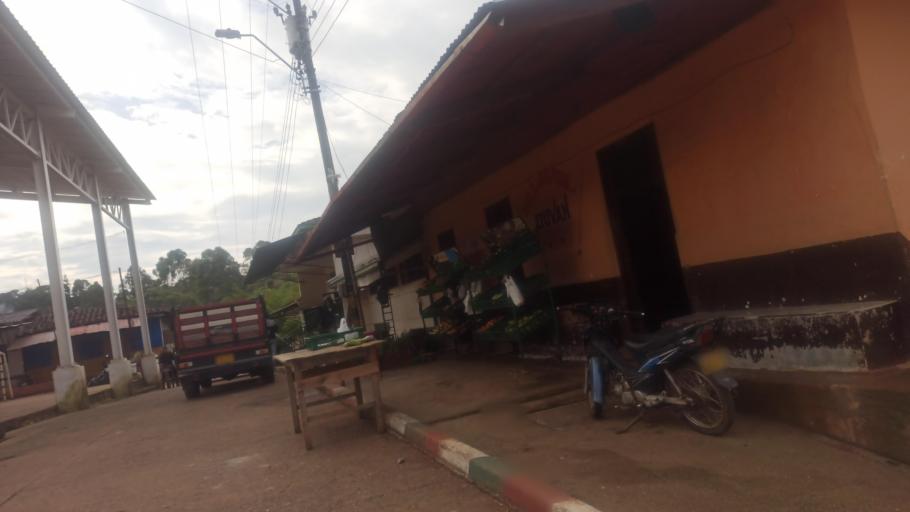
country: CO
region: Valle del Cauca
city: Jamundi
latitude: 3.1856
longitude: -76.6749
